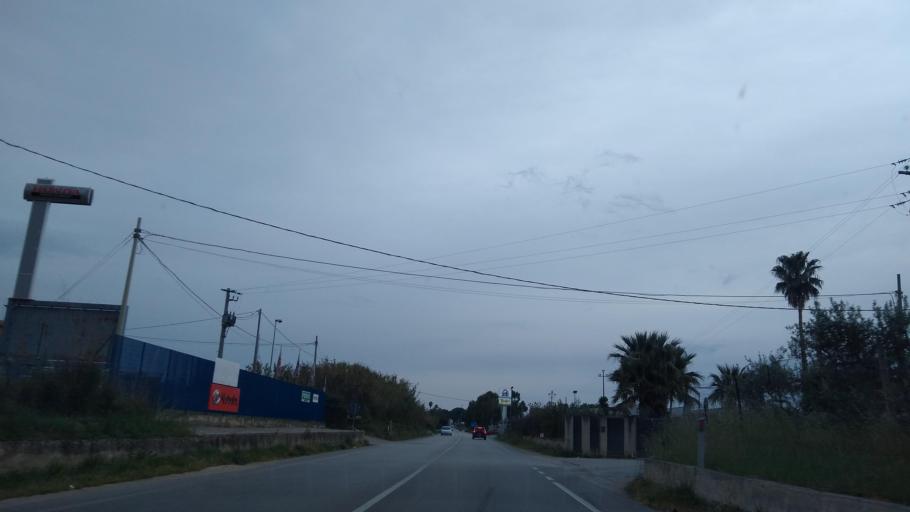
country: IT
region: Sicily
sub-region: Palermo
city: Partinico
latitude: 38.0314
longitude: 13.0951
